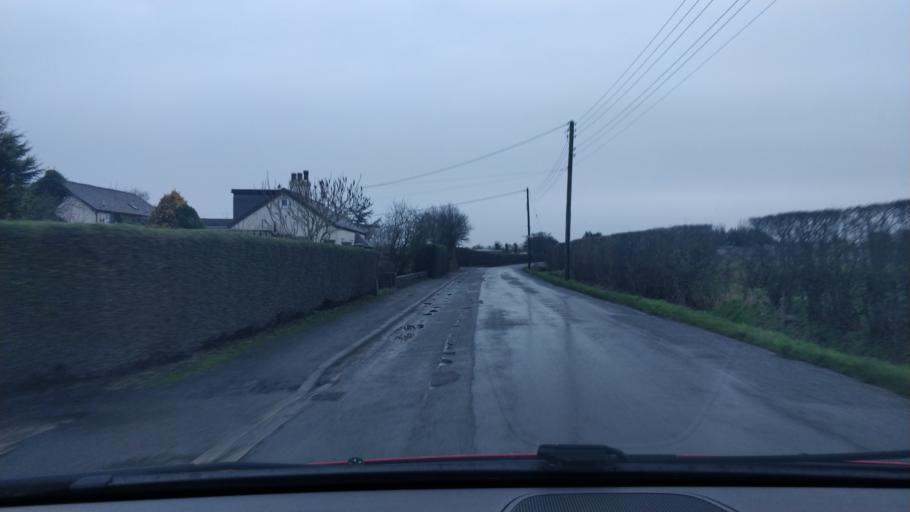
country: GB
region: England
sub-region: Lancashire
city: Tarleton
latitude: 53.6787
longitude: -2.8473
